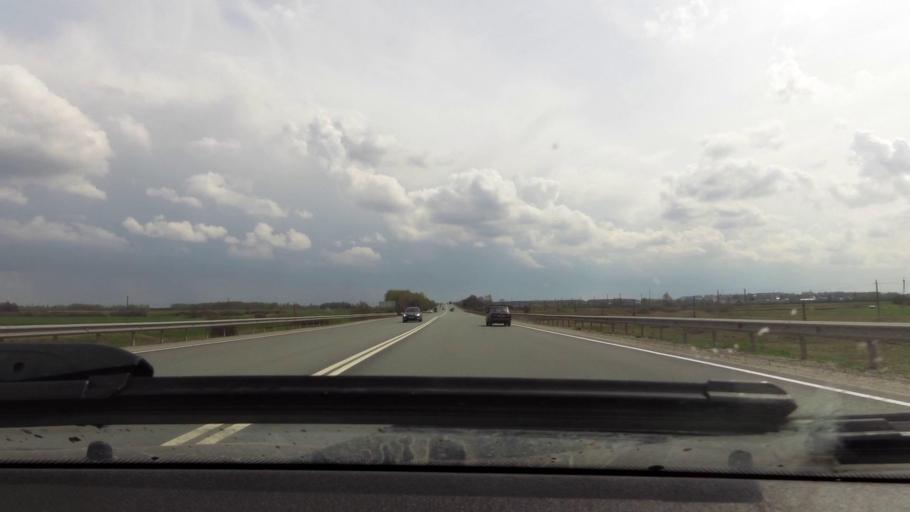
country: RU
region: Rjazan
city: Bagramovo
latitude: 54.7422
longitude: 39.4410
